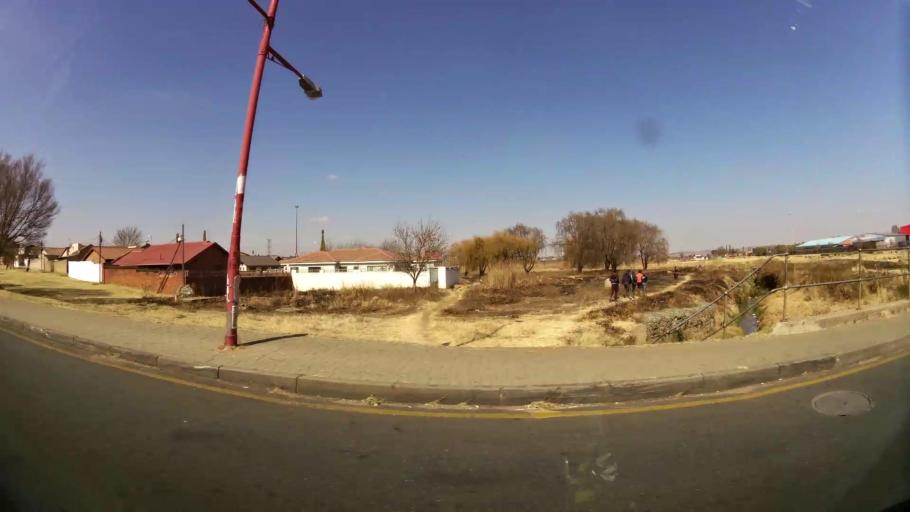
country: ZA
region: Gauteng
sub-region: City of Johannesburg Metropolitan Municipality
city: Soweto
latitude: -26.2641
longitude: 27.8811
